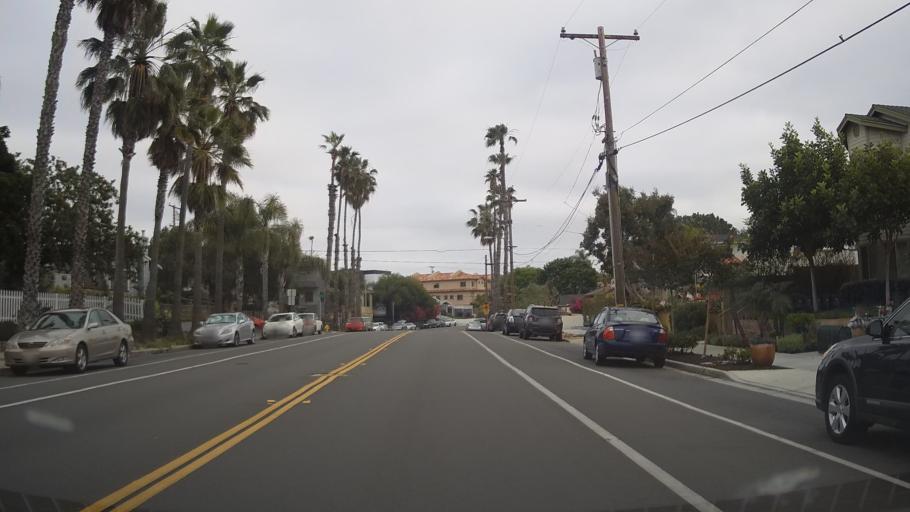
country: US
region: California
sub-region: San Diego County
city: San Diego
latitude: 32.7541
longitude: -117.1512
